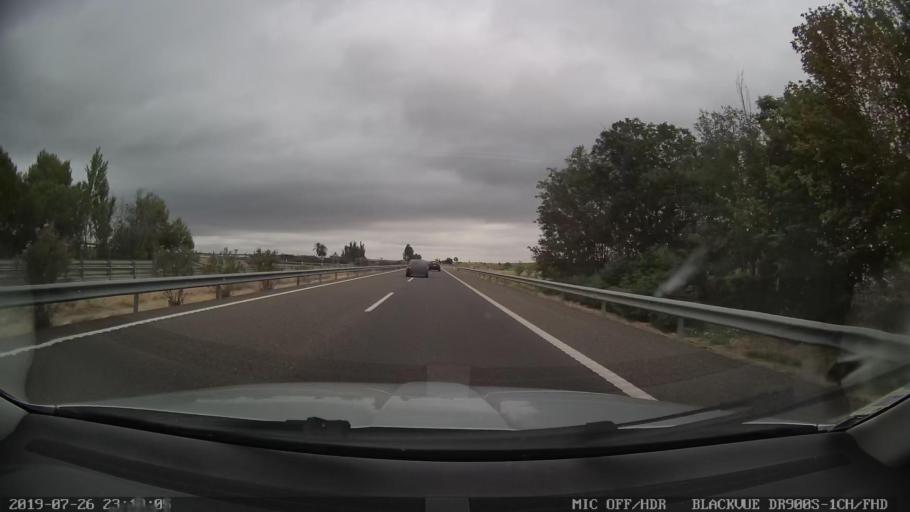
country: ES
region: Extremadura
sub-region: Provincia de Caceres
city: Almoharin
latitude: 39.1032
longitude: -5.9995
